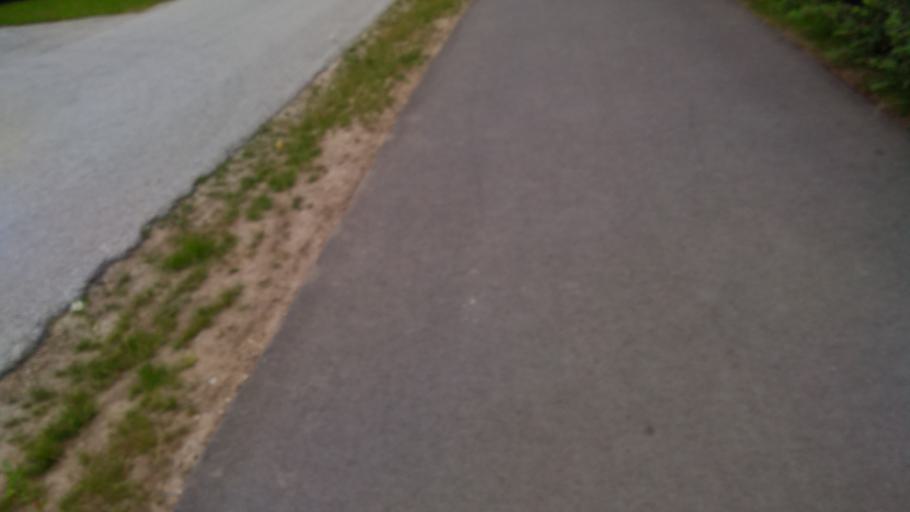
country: EE
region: Harju
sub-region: Viimsi vald
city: Viimsi
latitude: 59.5002
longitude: 24.8578
